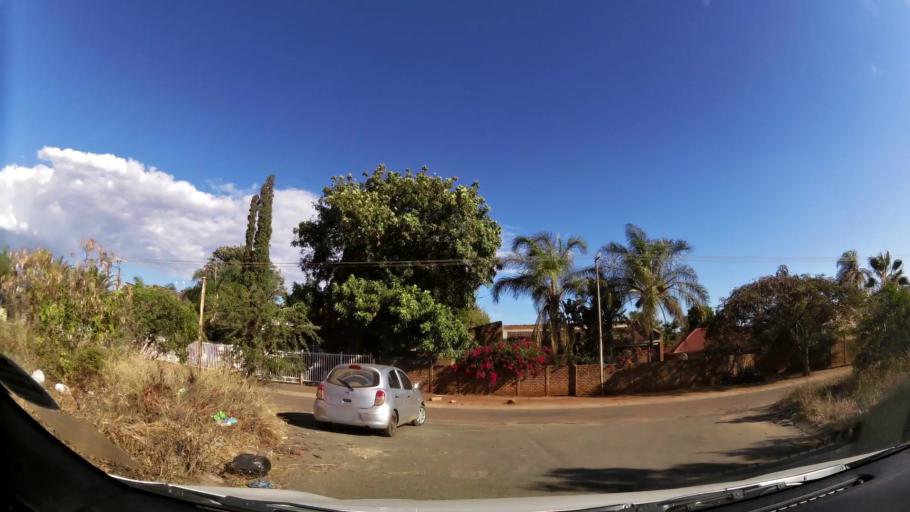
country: ZA
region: Limpopo
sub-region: Waterberg District Municipality
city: Mokopane
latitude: -24.1767
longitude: 28.9968
